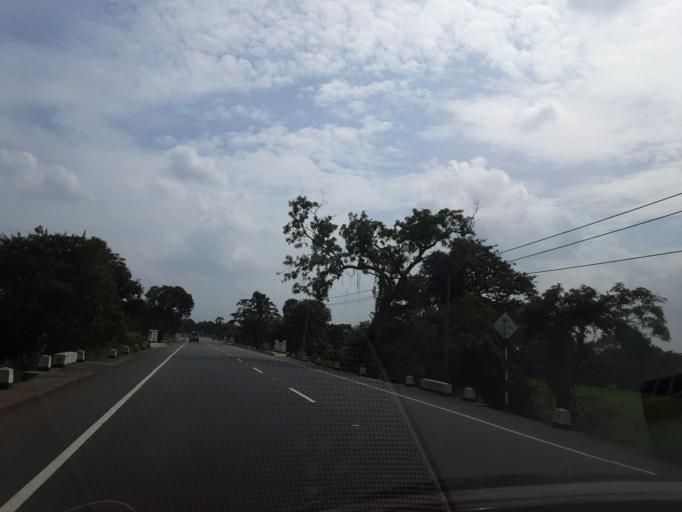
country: LK
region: North Central
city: Anuradhapura
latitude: 8.5094
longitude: 80.5064
